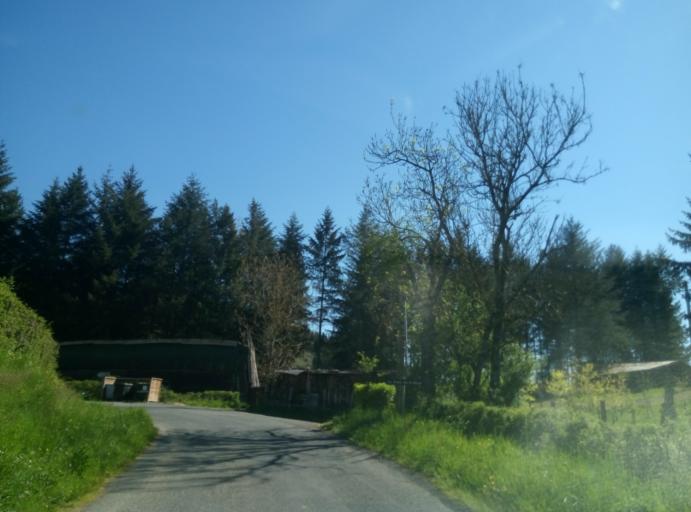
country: FR
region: Rhone-Alpes
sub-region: Departement du Rhone
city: Grandris
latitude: 46.0484
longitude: 4.4967
